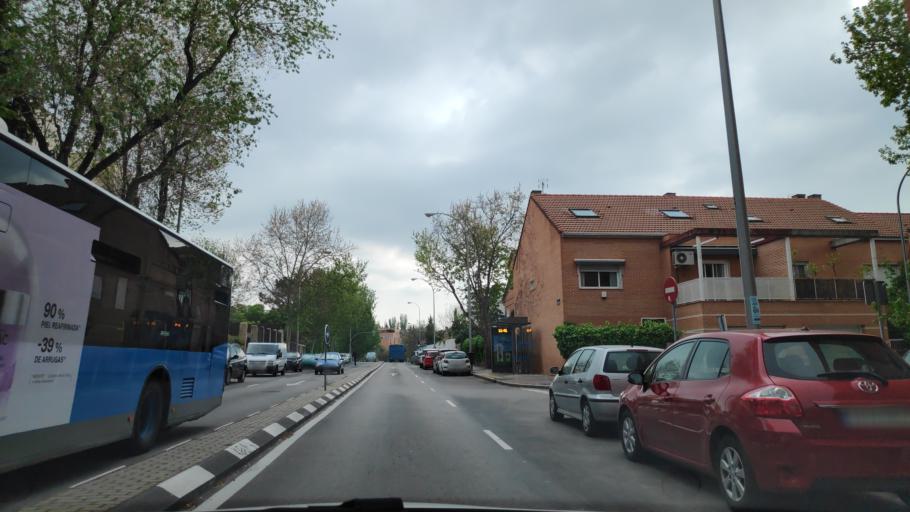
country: ES
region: Madrid
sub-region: Provincia de Madrid
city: Pozuelo de Alarcon
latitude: 40.4559
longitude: -3.7840
